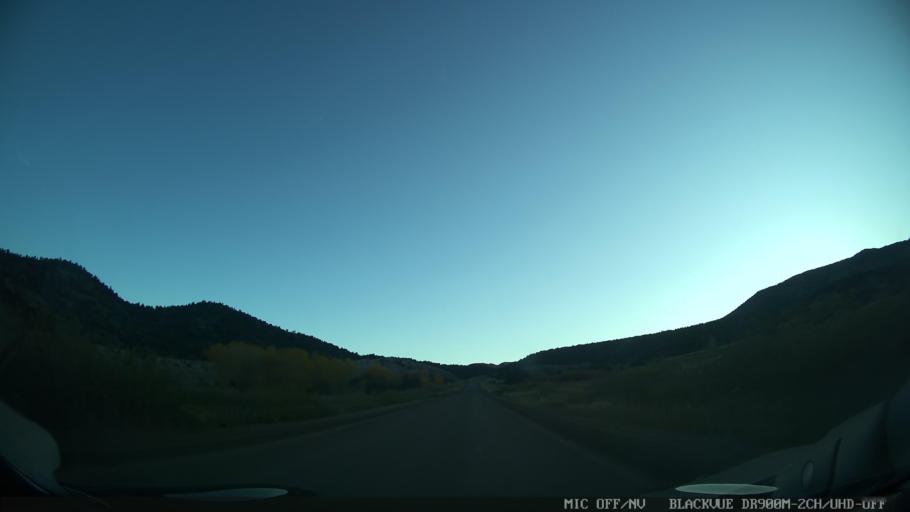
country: US
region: Colorado
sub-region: Grand County
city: Kremmling
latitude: 39.9028
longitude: -106.5901
